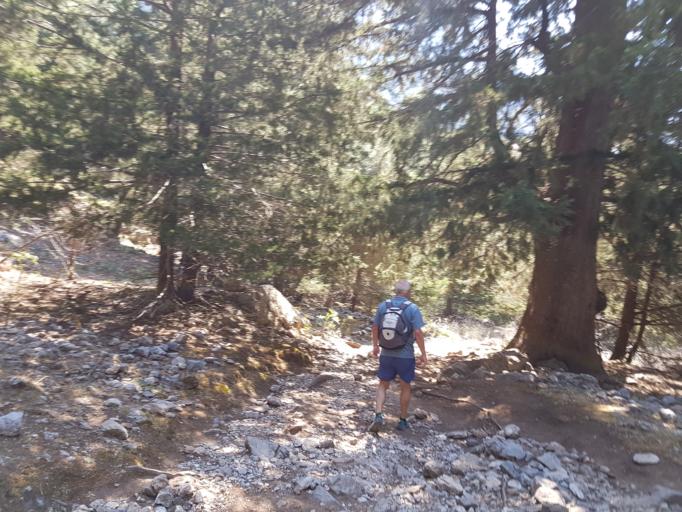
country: GR
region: Crete
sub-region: Nomos Chanias
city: Perivolia
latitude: 35.3065
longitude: 23.9366
